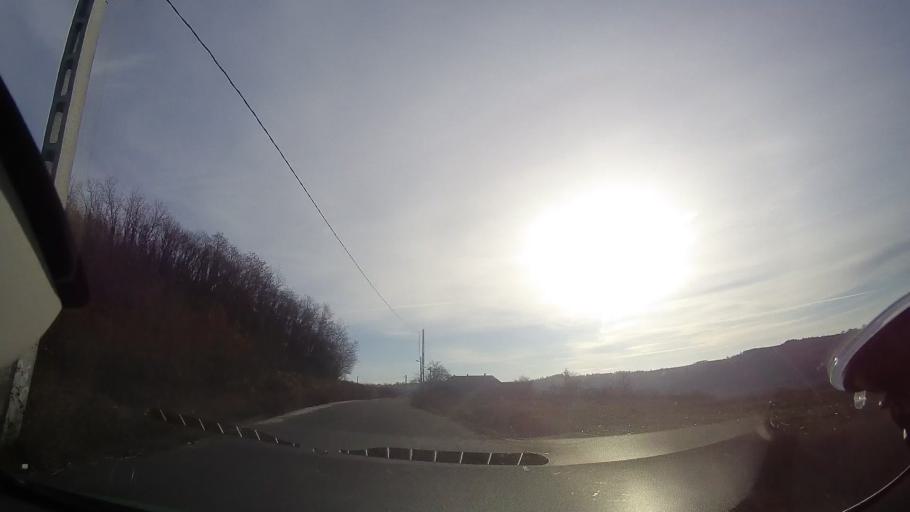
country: RO
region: Bihor
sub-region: Comuna Sarbi
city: Burzuc
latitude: 47.1358
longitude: 22.1858
